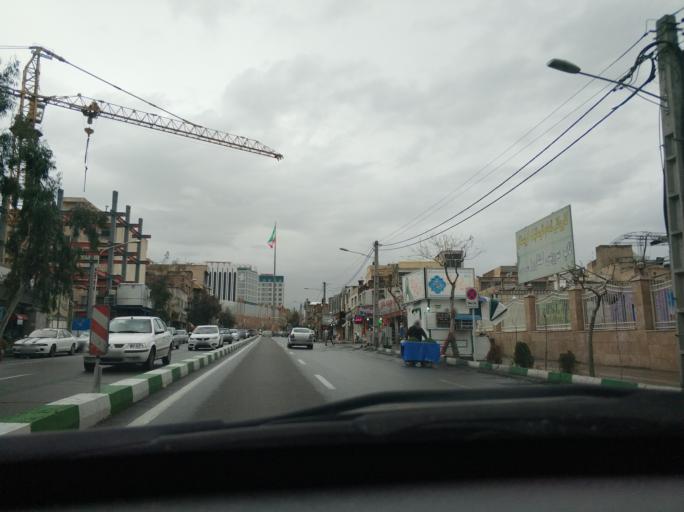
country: IR
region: Tehran
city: Tehran
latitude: 35.7046
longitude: 51.4396
